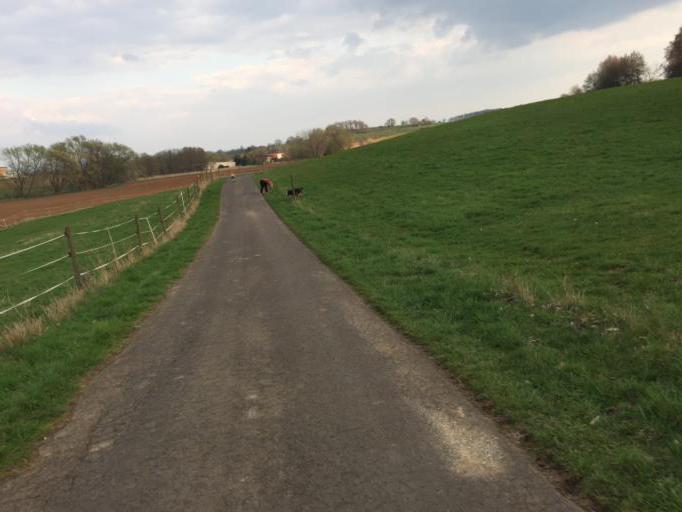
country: DE
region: Hesse
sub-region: Regierungsbezirk Giessen
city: Laubach
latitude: 50.5432
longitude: 8.9584
